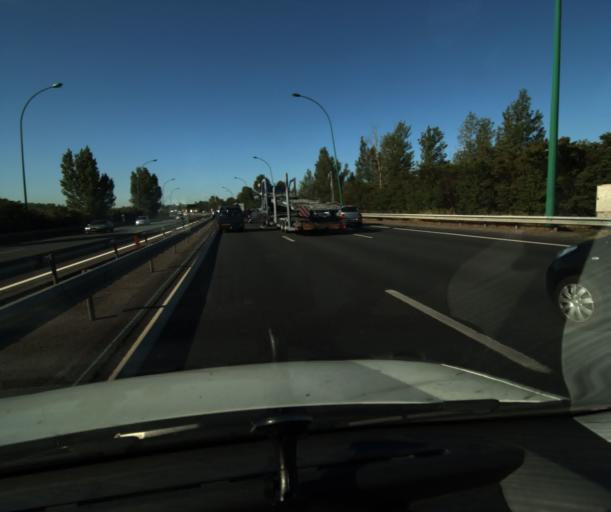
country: FR
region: Midi-Pyrenees
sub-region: Departement de la Haute-Garonne
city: Ramonville-Saint-Agne
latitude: 43.5723
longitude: 1.4947
